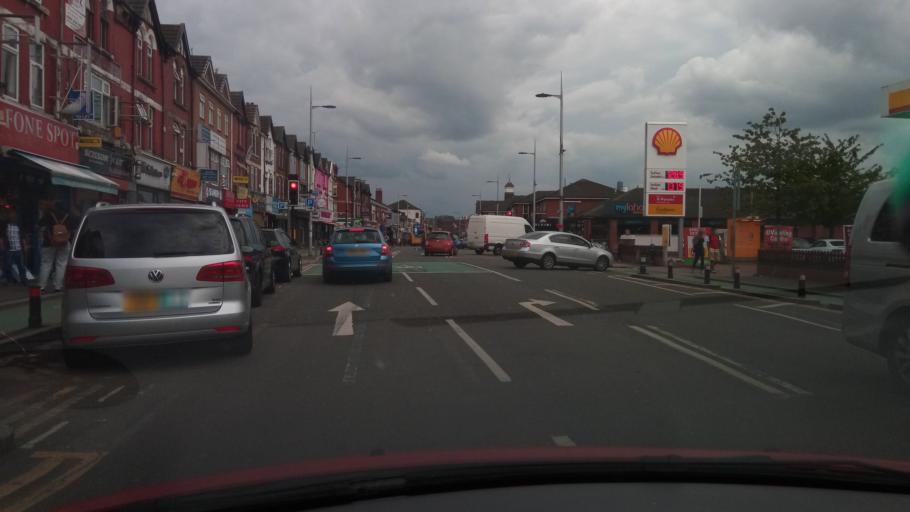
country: GB
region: England
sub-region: Manchester
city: Fallowfield
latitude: 53.4567
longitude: -2.2261
